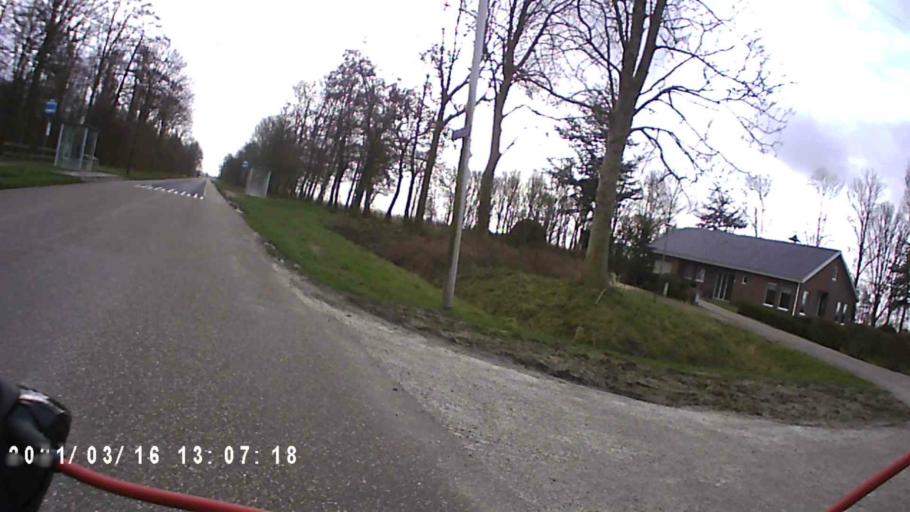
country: NL
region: Friesland
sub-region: Gemeente Het Bildt
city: Minnertsga
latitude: 53.2511
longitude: 5.6195
